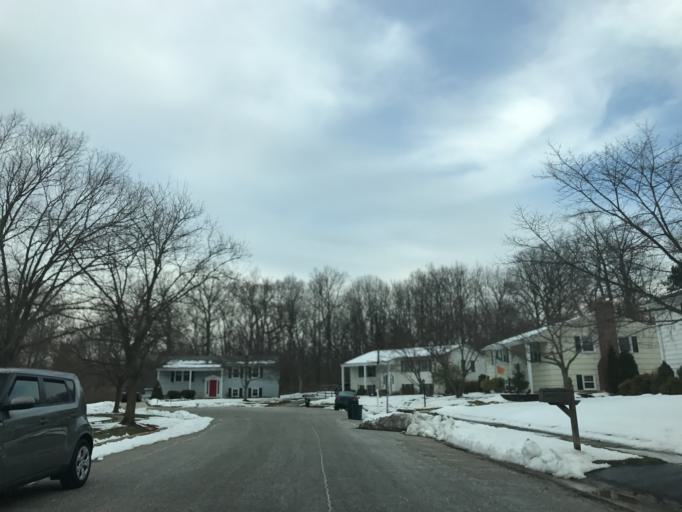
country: US
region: Maryland
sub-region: Baltimore County
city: Lutherville
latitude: 39.4156
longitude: -76.6424
